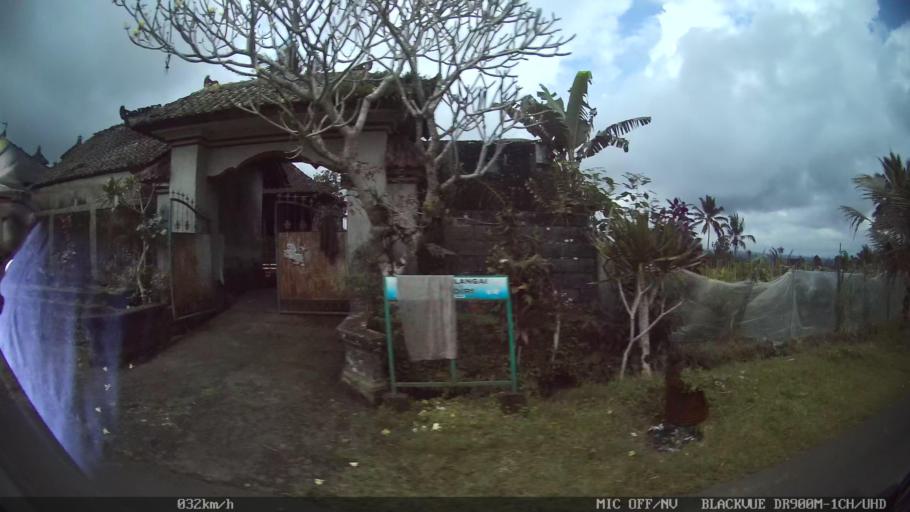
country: ID
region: Bali
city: Peneng
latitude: -8.3546
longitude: 115.2081
